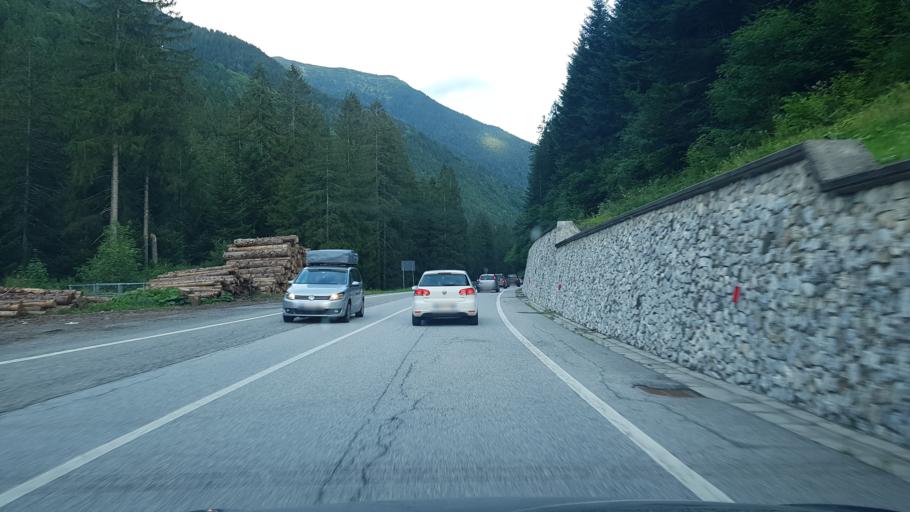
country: IT
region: Friuli Venezia Giulia
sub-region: Provincia di Udine
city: Rigolato
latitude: 46.5666
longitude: 12.8348
